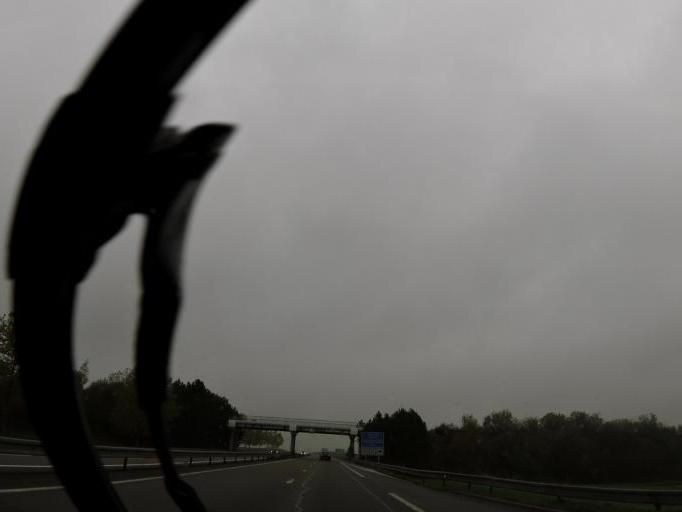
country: FR
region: Champagne-Ardenne
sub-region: Departement de la Marne
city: Courtisols
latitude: 49.0316
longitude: 4.4709
